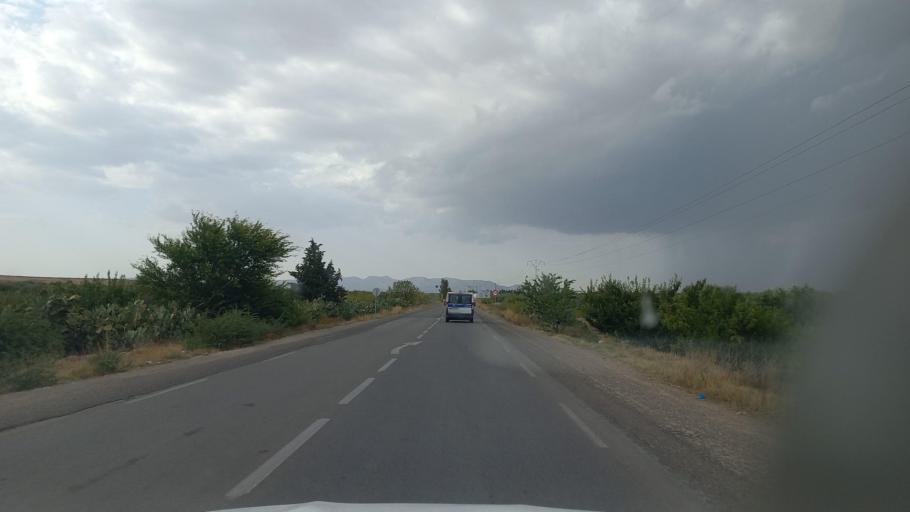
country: TN
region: Al Qasrayn
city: Sbiba
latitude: 35.3052
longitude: 9.0870
